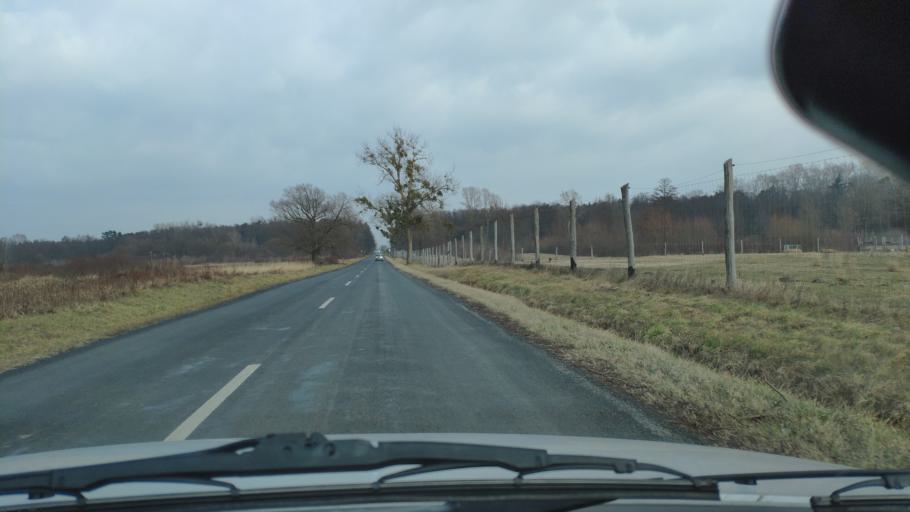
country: HU
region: Zala
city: Nagykanizsa
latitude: 46.4441
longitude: 16.9284
